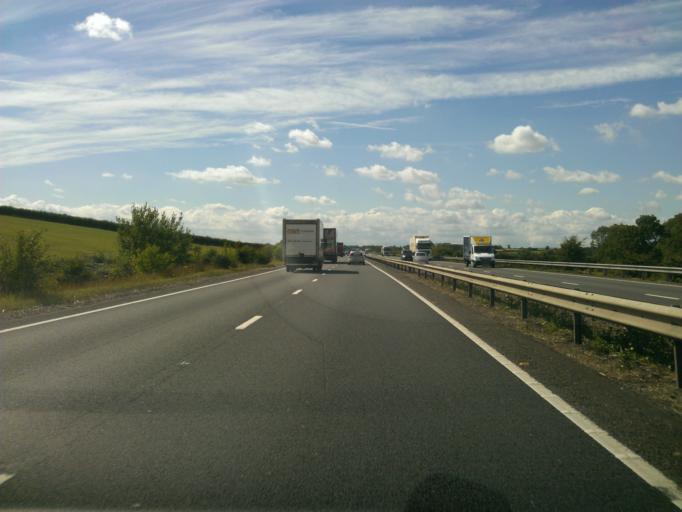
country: GB
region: England
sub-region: Bedford
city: Pertenhall
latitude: 52.3616
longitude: -0.4123
